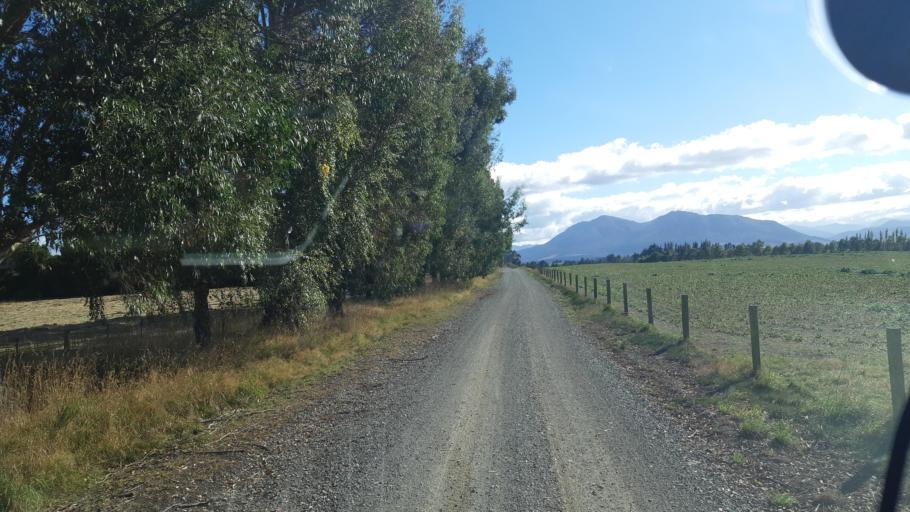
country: NZ
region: Southland
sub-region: Southland District
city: Winton
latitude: -45.7028
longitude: 168.1893
